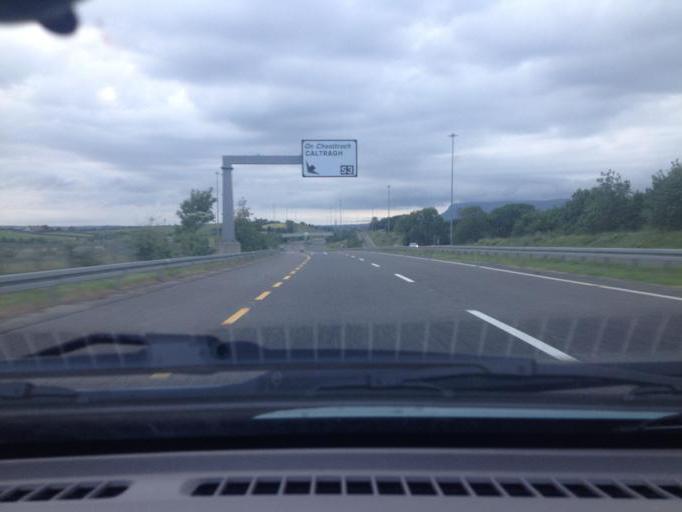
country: IE
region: Connaught
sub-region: Sligo
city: Sligo
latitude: 54.2553
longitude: -8.4785
